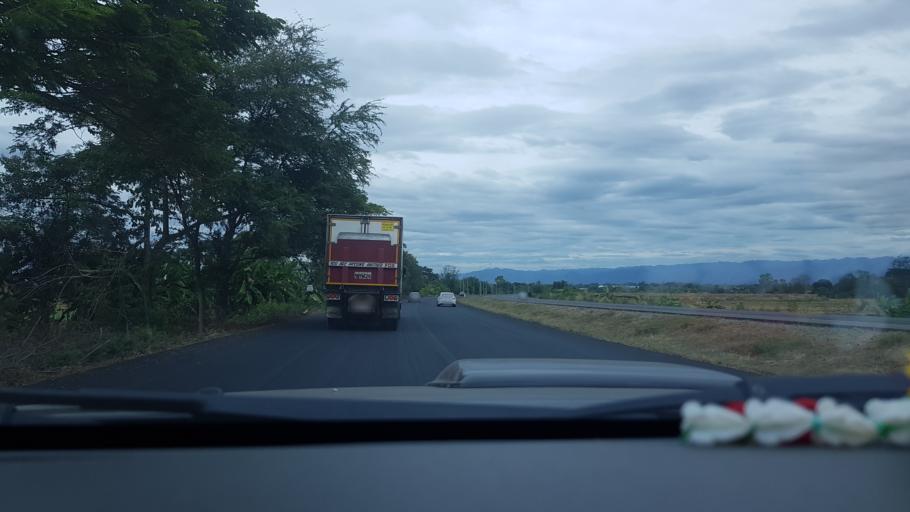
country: TH
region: Phetchabun
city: Phetchabun
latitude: 16.4934
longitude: 101.1439
